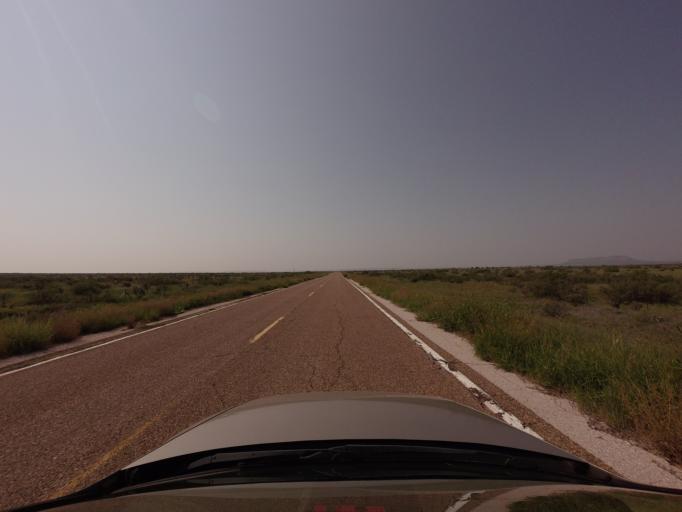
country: US
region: New Mexico
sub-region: Quay County
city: Tucumcari
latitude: 34.9862
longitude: -103.7484
